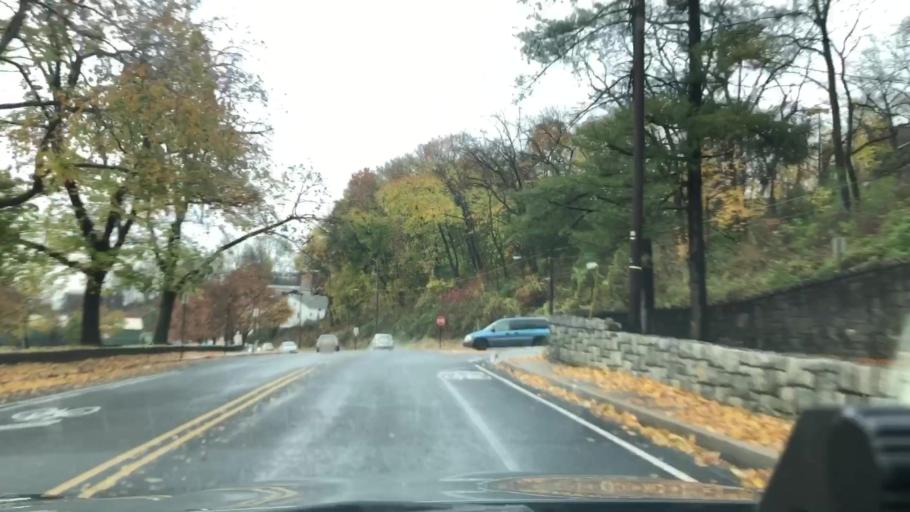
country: US
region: Pennsylvania
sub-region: Lehigh County
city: Allentown
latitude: 40.5972
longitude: -75.4781
